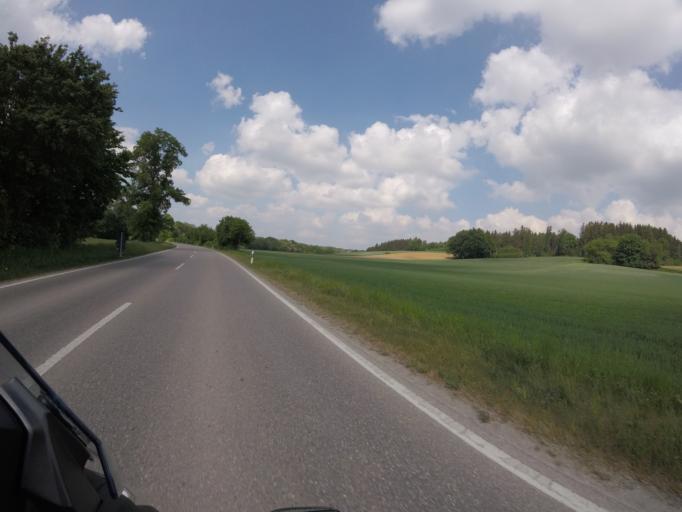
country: DE
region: Bavaria
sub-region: Upper Bavaria
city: Wolfersdorf
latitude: 48.4605
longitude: 11.6920
